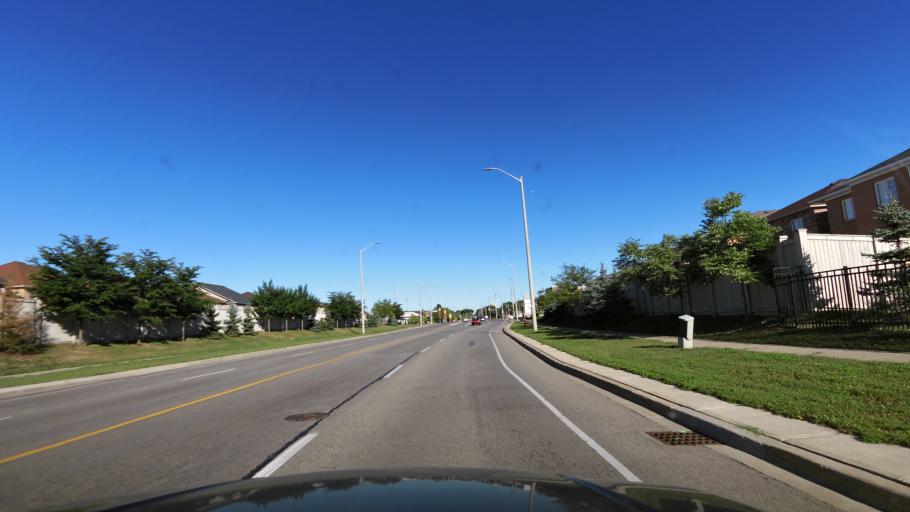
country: CA
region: Ontario
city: Mississauga
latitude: 43.5958
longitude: -79.6617
